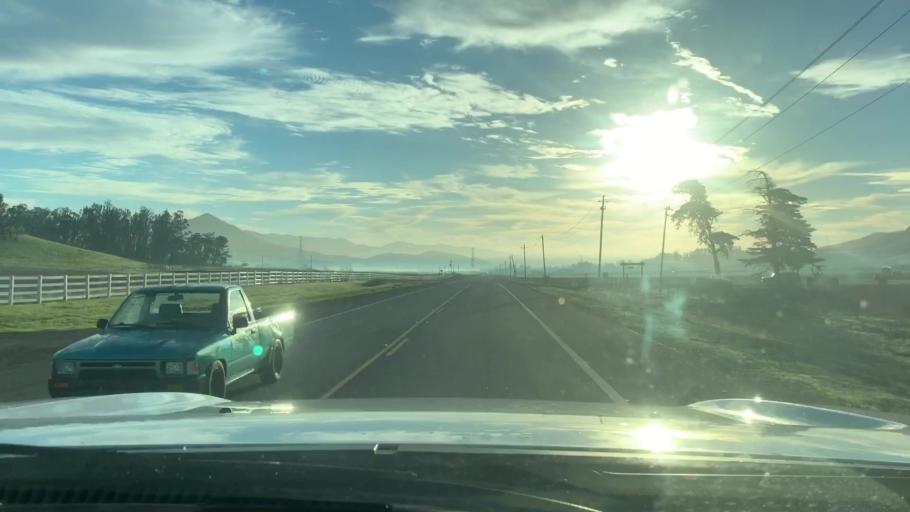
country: US
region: California
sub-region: San Luis Obispo County
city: San Luis Obispo
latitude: 35.2865
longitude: -120.7382
